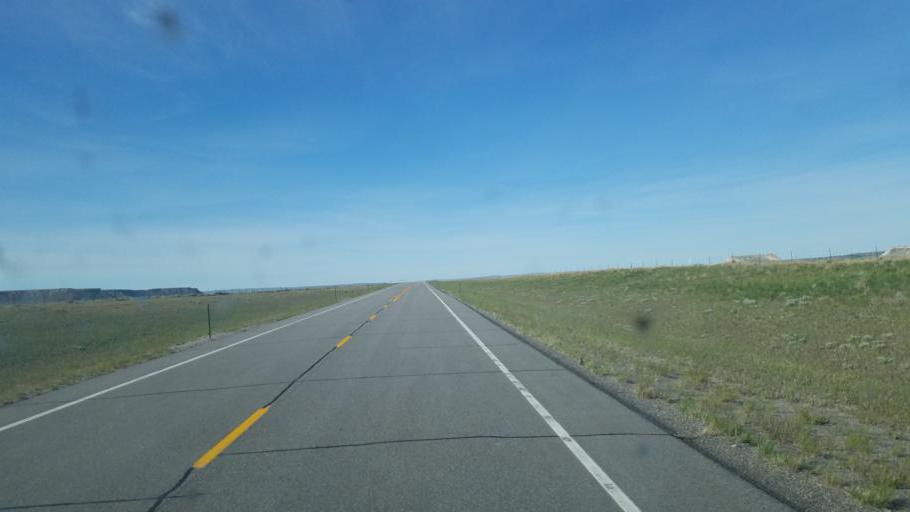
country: US
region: Wyoming
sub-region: Fremont County
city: Riverton
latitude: 42.6656
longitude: -108.1833
